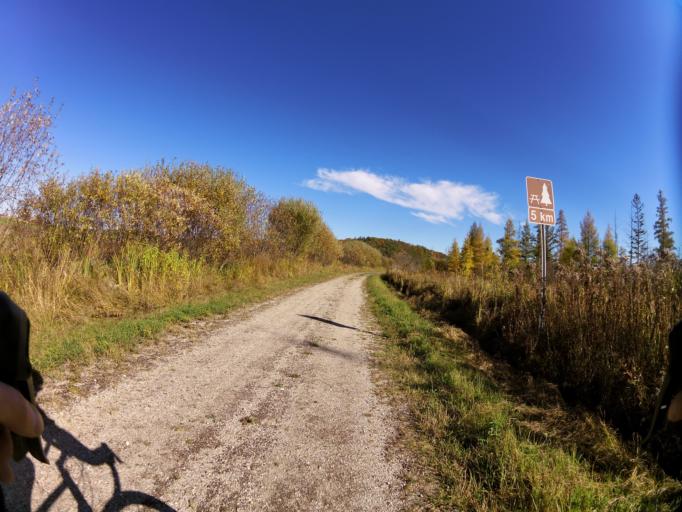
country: CA
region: Quebec
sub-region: Outaouais
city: Wakefield
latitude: 45.8662
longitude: -76.0185
